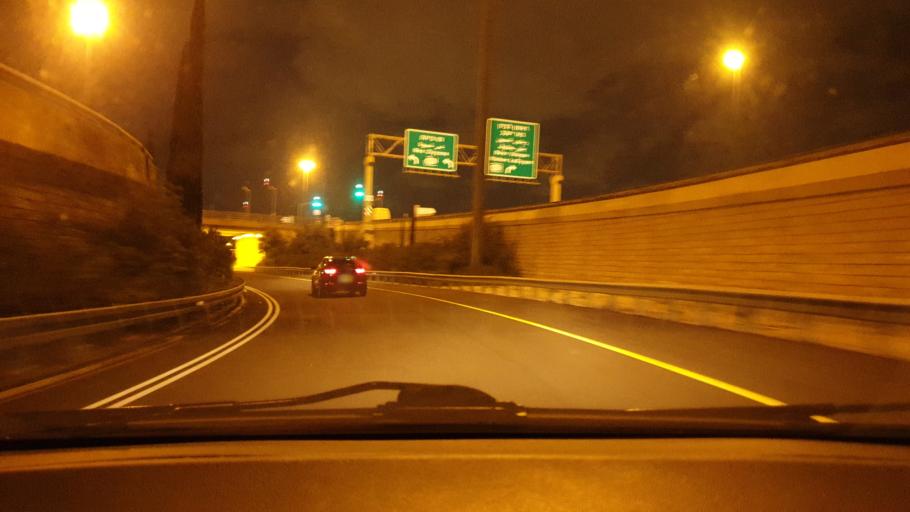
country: IL
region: Central District
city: Ness Ziona
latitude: 31.9393
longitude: 34.8175
